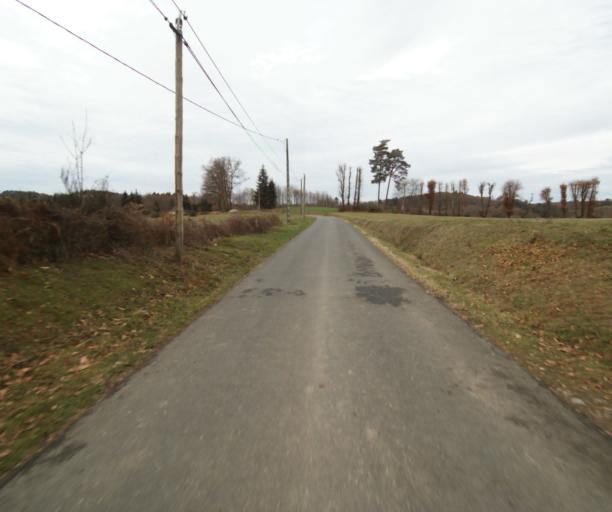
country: FR
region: Limousin
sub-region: Departement de la Correze
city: Chameyrat
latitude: 45.2346
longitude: 1.6815
